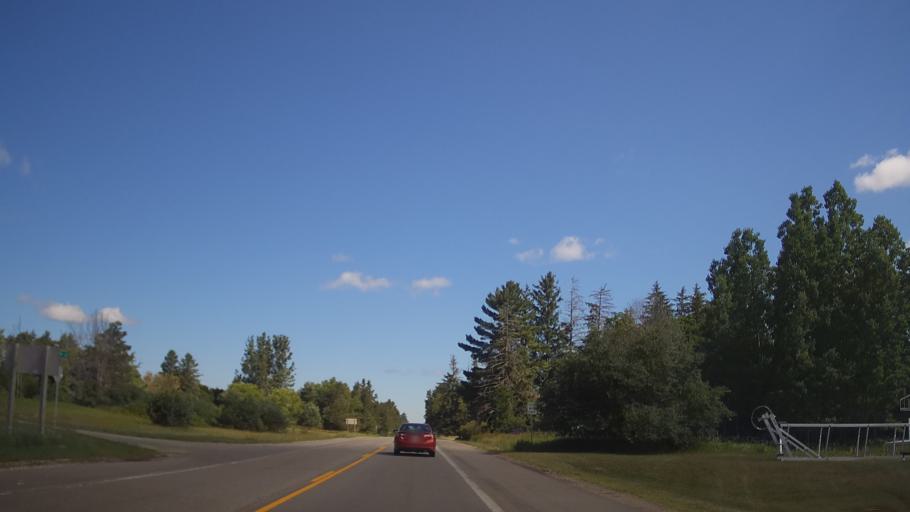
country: US
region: Michigan
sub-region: Cheboygan County
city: Indian River
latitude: 45.4950
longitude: -84.7812
